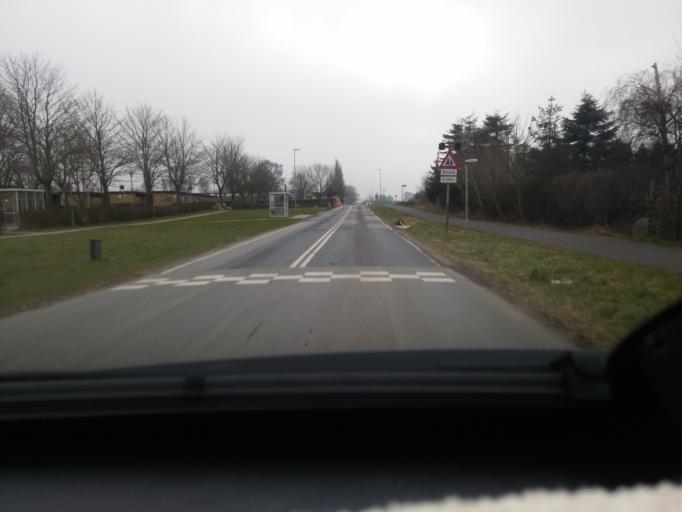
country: DK
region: South Denmark
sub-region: Nyborg Kommune
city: Ullerslev
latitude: 55.3638
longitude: 10.7261
